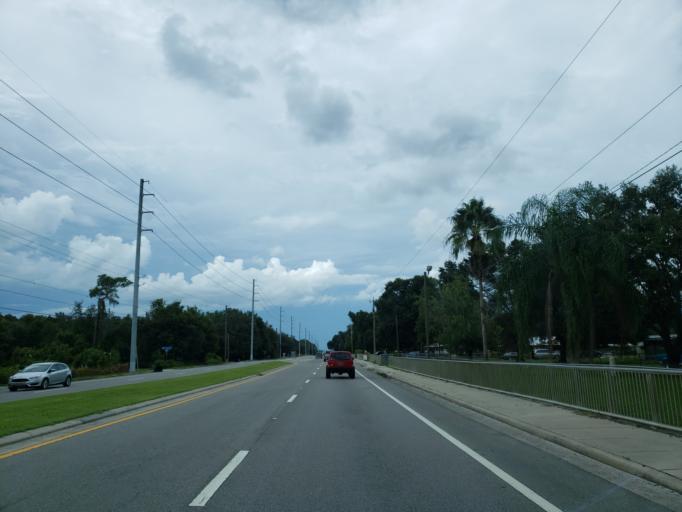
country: US
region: Florida
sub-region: Polk County
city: Willow Oak
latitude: 27.9426
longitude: -82.0552
